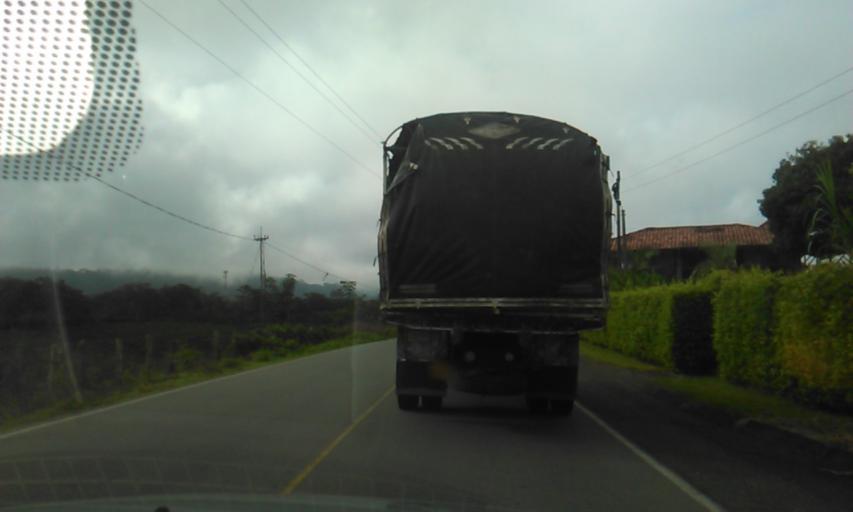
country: CO
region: Quindio
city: Cordoba
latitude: 4.4352
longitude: -75.7168
